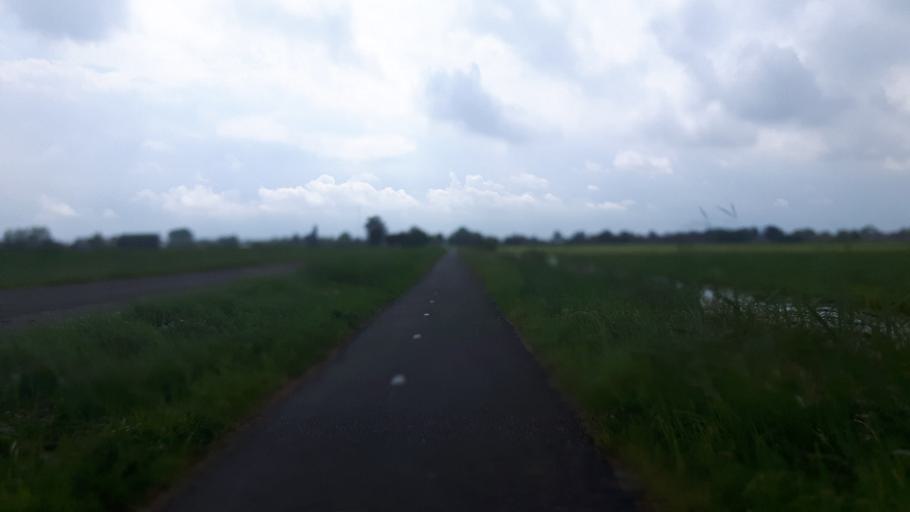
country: NL
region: Utrecht
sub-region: Gemeente Oudewater
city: Oudewater
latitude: 52.0019
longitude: 4.8991
